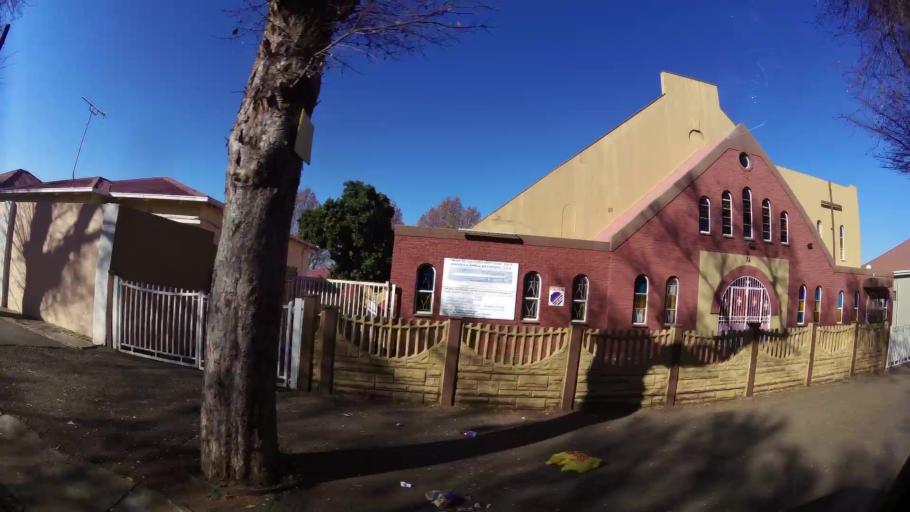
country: ZA
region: Gauteng
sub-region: City of Johannesburg Metropolitan Municipality
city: Johannesburg
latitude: -26.2012
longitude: 28.1030
